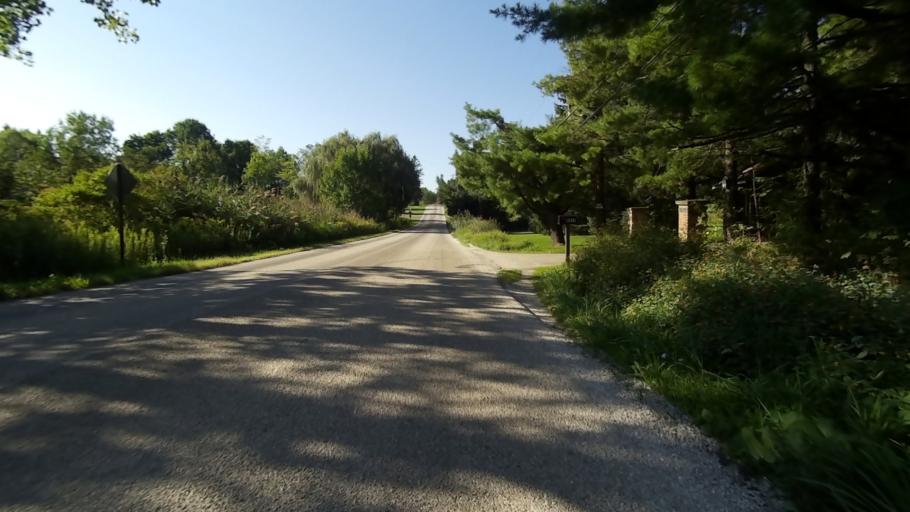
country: US
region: Ohio
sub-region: Portage County
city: Mantua
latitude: 41.2582
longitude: -81.2826
